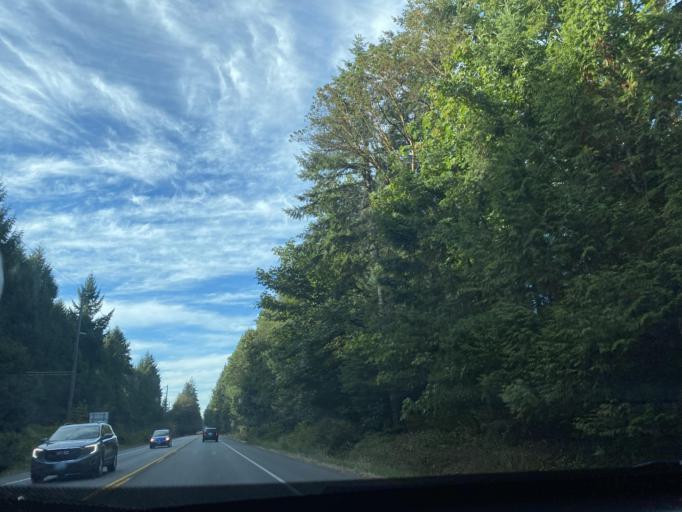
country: US
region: Washington
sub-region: Kitsap County
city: Suquamish
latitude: 47.6807
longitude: -122.5406
